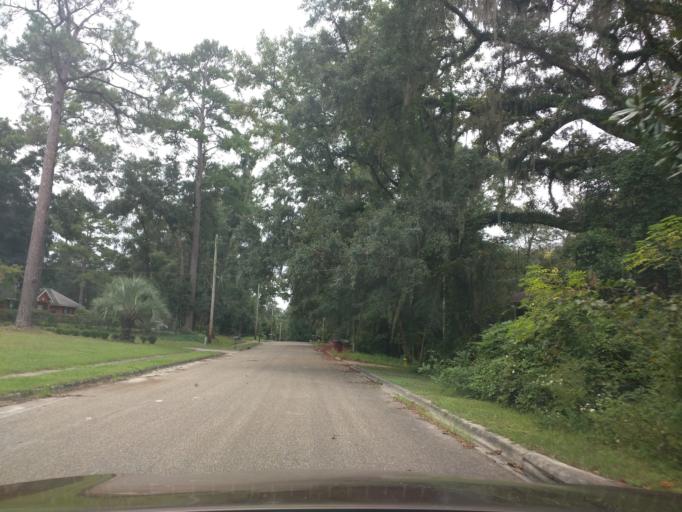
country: US
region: Florida
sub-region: Leon County
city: Tallahassee
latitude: 30.4621
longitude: -84.2348
